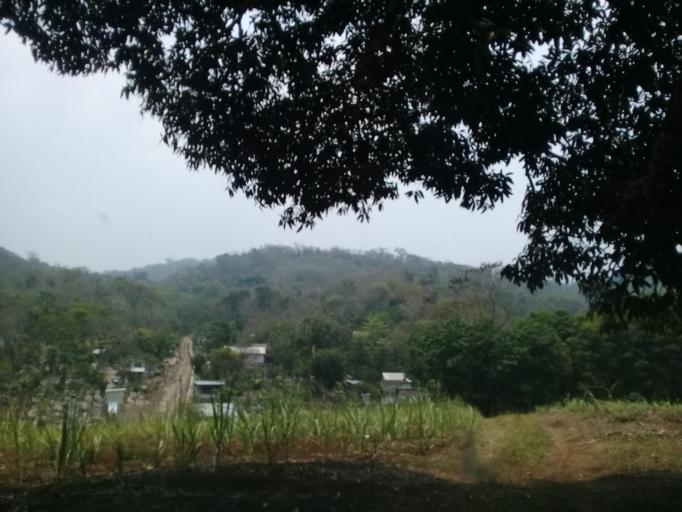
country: MX
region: Veracruz
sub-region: Tezonapa
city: Laguna Chica (Pueblo Nuevo)
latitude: 18.5372
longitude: -96.7291
